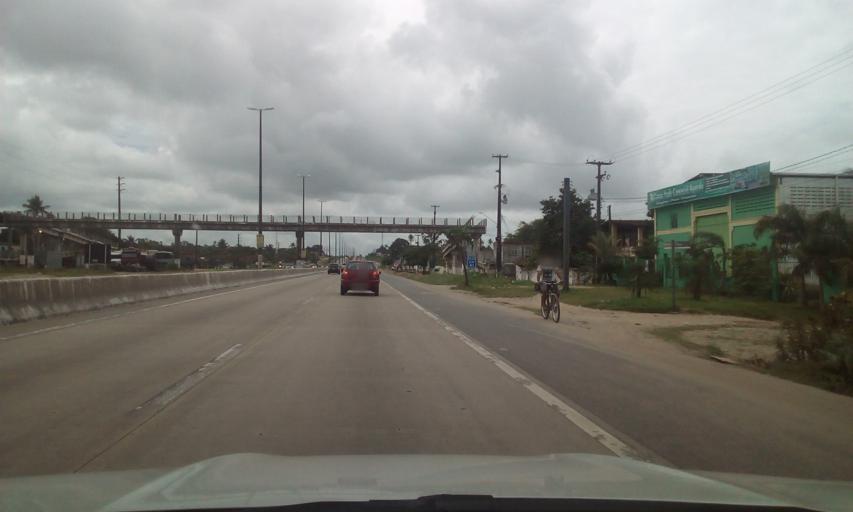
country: BR
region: Pernambuco
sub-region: Igarassu
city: Igarassu
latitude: -7.8286
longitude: -34.9146
